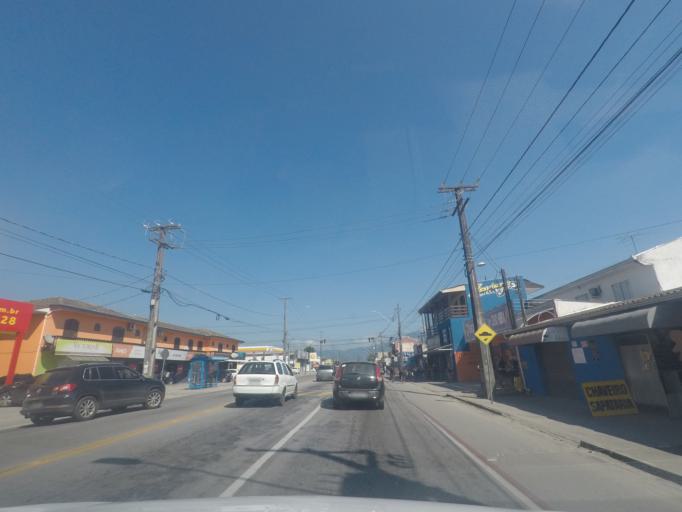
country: BR
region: Parana
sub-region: Paranagua
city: Paranagua
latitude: -25.5591
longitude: -48.5596
